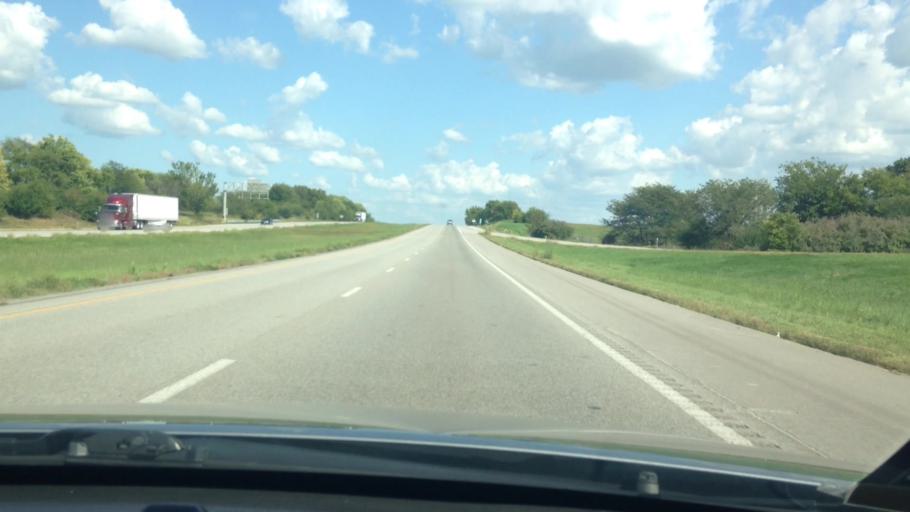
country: US
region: Missouri
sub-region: Clay County
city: Smithville
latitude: 39.3111
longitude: -94.5546
